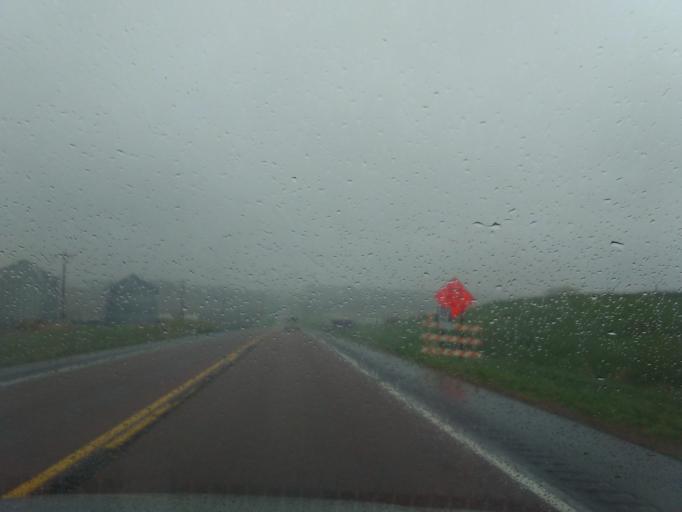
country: US
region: Nebraska
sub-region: Wayne County
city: Wayne
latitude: 42.2355
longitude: -97.1614
